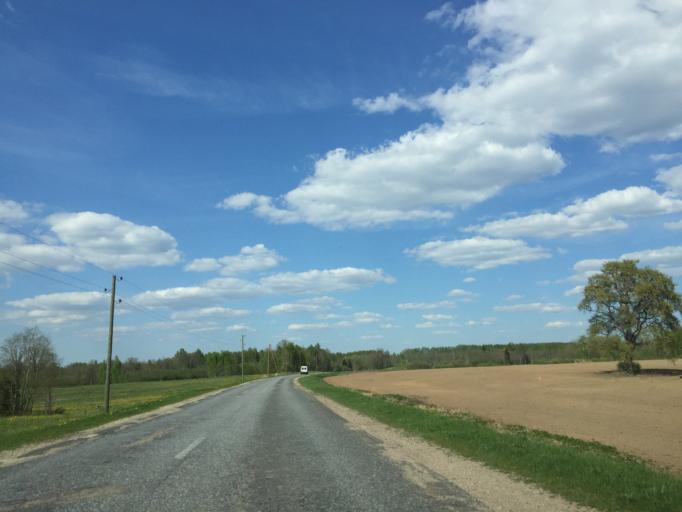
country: LV
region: Limbazu Rajons
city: Limbazi
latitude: 57.4337
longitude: 24.7155
